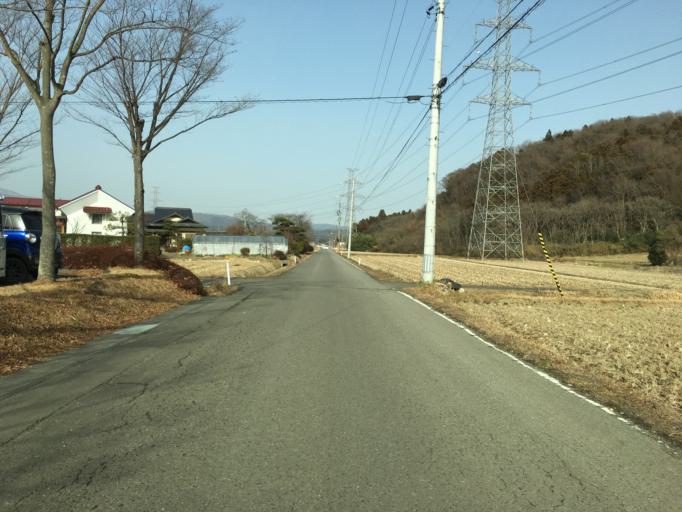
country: JP
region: Fukushima
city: Motomiya
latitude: 37.5472
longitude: 140.3945
